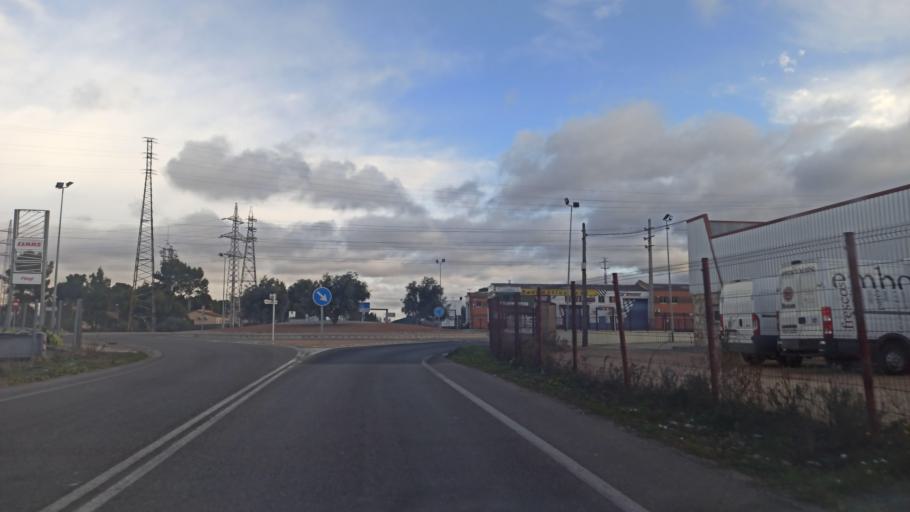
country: ES
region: Catalonia
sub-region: Provincia de Lleida
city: Alcoletge
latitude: 41.6298
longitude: 0.6635
